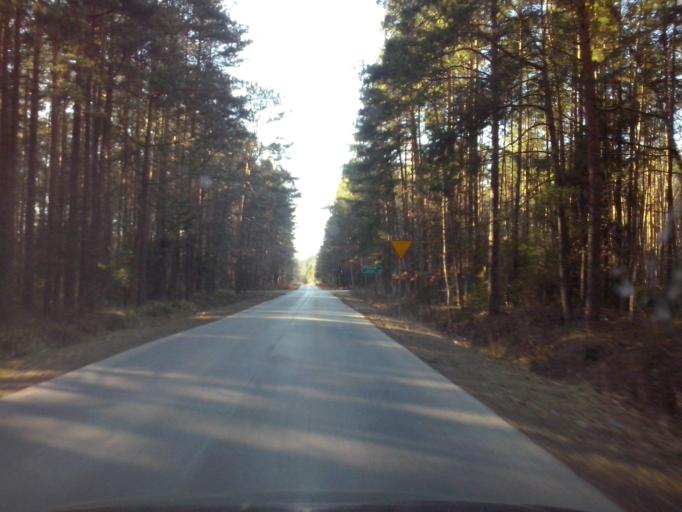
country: PL
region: Subcarpathian Voivodeship
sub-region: Powiat nizanski
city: Harasiuki
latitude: 50.5320
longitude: 22.4497
